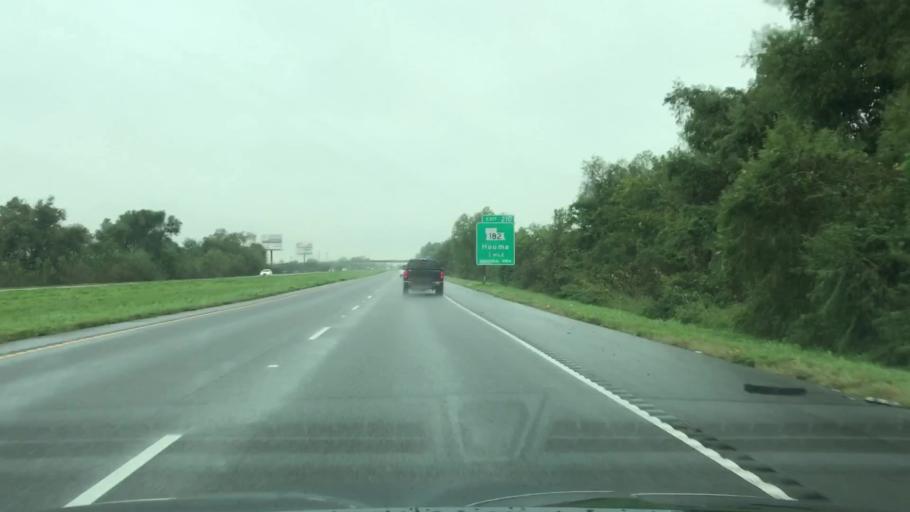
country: US
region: Louisiana
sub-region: Lafourche Parish
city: Raceland
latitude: 29.6899
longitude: -90.6150
